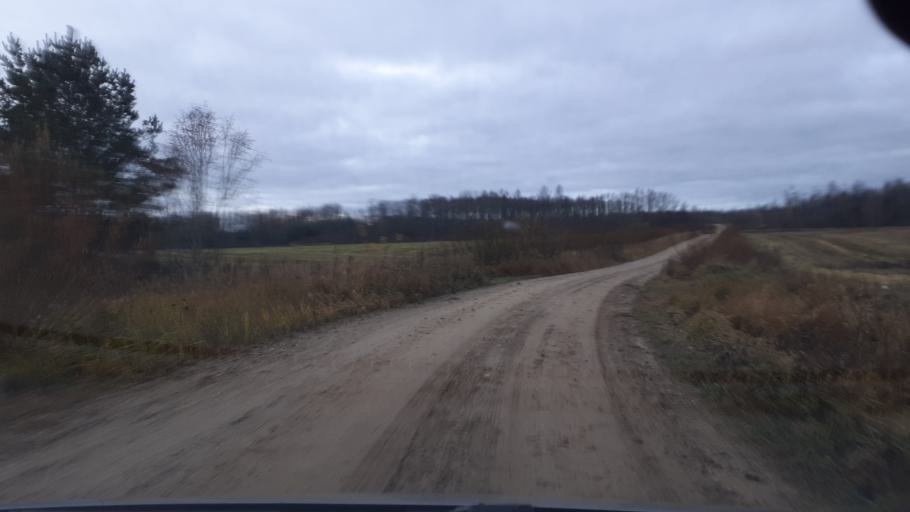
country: LV
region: Kuldigas Rajons
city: Kuldiga
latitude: 57.0053
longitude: 21.9279
